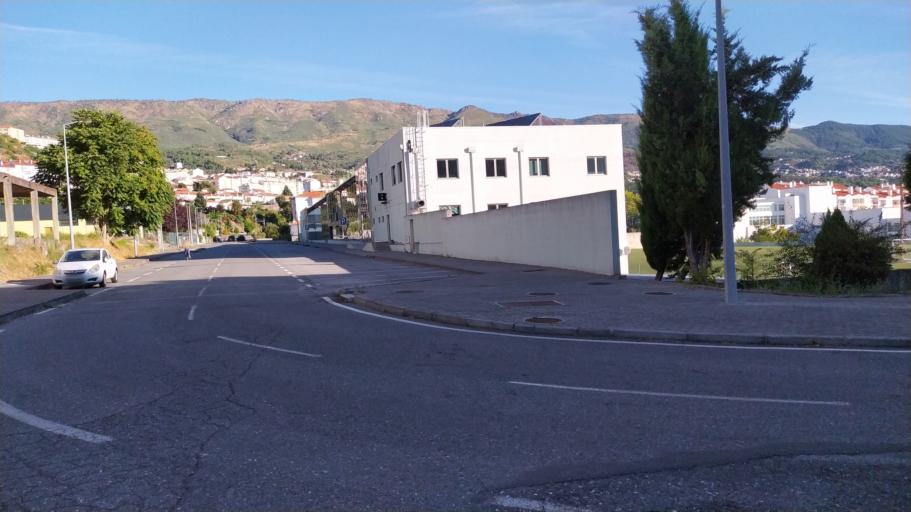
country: PT
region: Castelo Branco
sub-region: Covilha
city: Covilha
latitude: 40.2775
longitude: -7.4933
